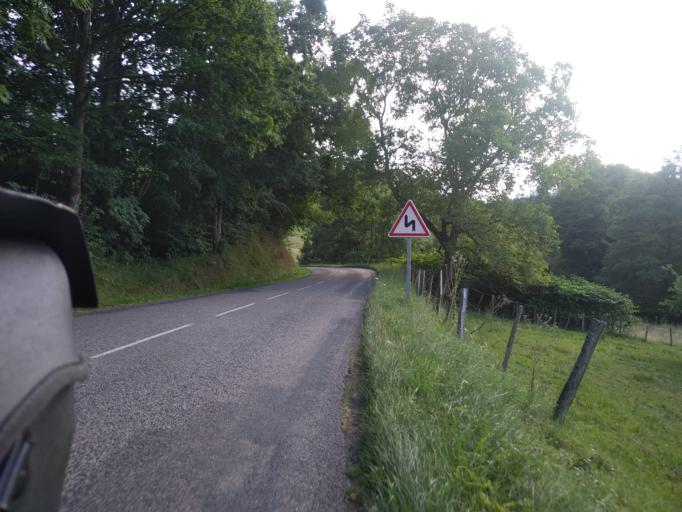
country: FR
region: Rhone-Alpes
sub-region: Departement du Rhone
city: Montrottier
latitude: 45.7879
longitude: 4.4956
